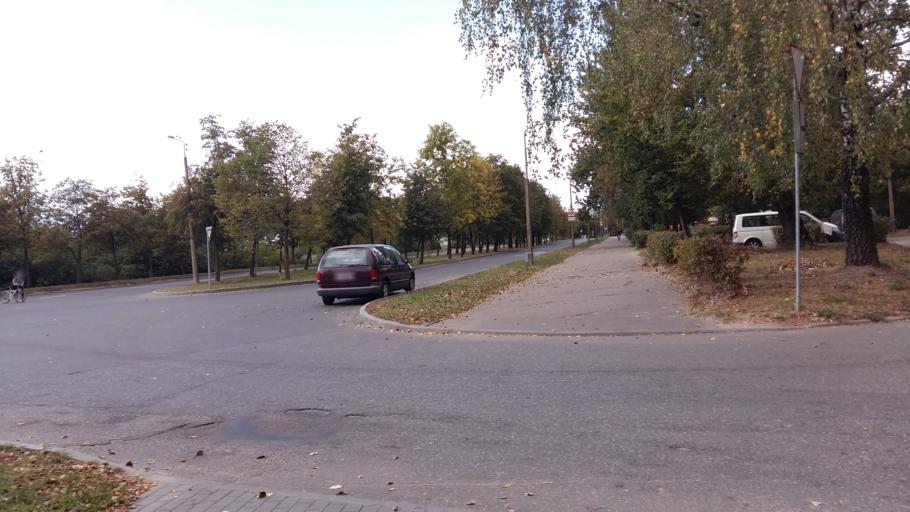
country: BY
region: Grodnenskaya
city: Hrodna
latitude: 53.7000
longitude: 23.7992
